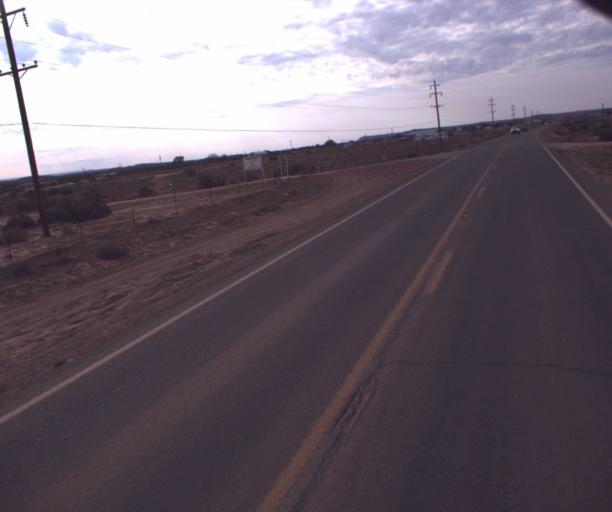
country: US
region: Arizona
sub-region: Apache County
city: Many Farms
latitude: 36.3606
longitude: -109.6149
